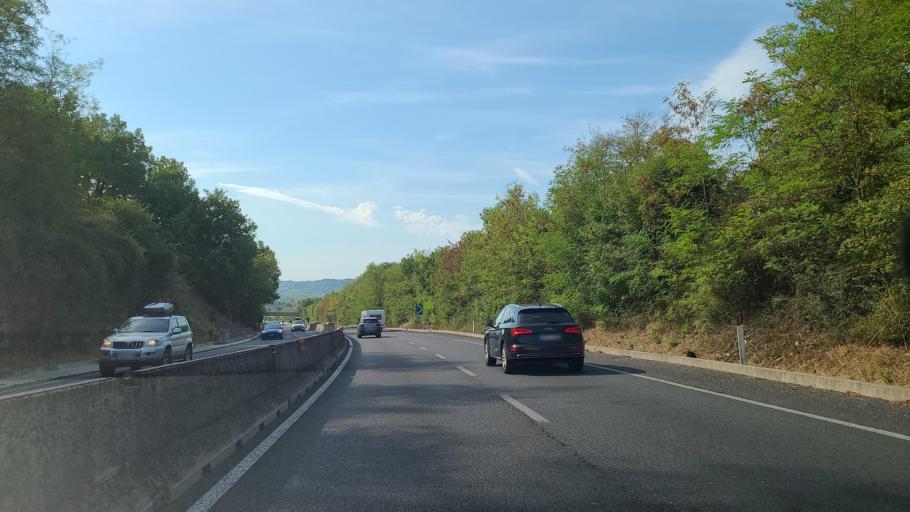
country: IT
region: Tuscany
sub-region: Province of Florence
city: San Casciano in Val di Pesa
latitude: 43.6423
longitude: 11.1781
